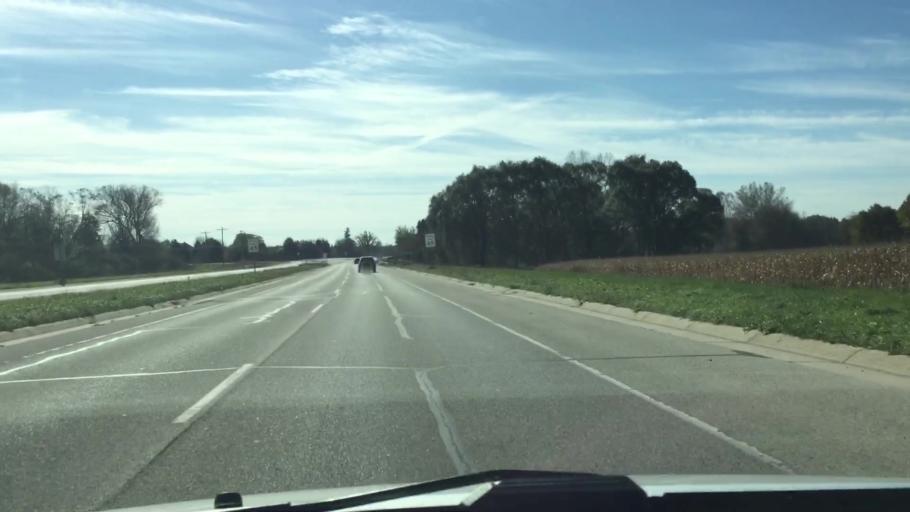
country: US
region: Wisconsin
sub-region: Waukesha County
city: Pewaukee
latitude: 43.1037
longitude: -88.2448
